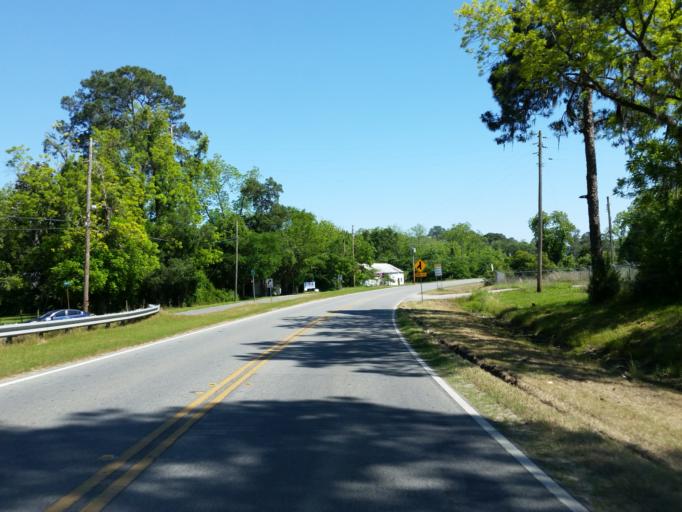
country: US
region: Georgia
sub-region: Cook County
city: Sparks
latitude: 31.1544
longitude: -83.4293
